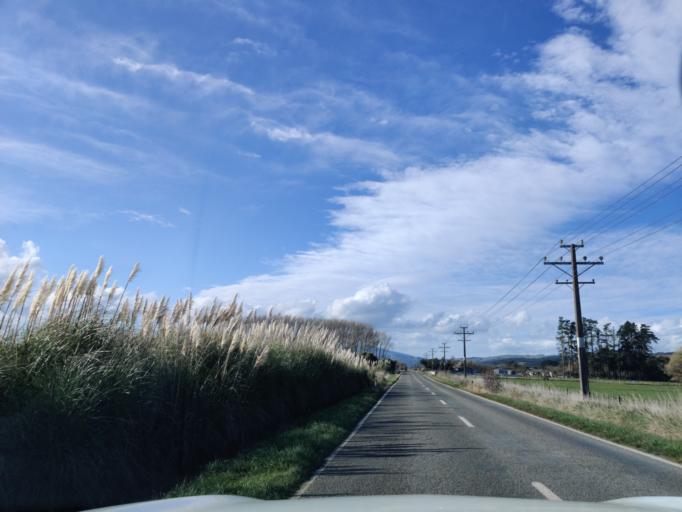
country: NZ
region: Manawatu-Wanganui
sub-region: Palmerston North City
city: Palmerston North
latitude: -40.3550
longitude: 175.6893
